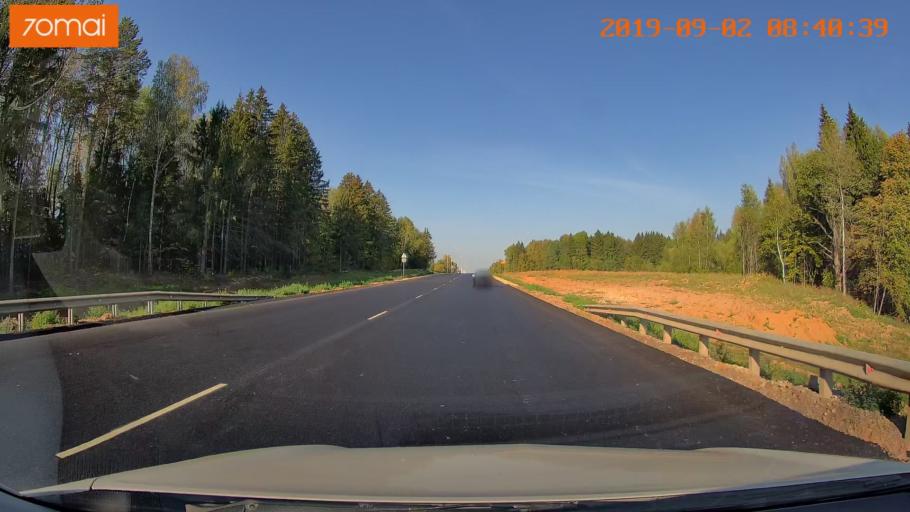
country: RU
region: Kaluga
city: Kudinovo
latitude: 54.9739
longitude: 36.1285
